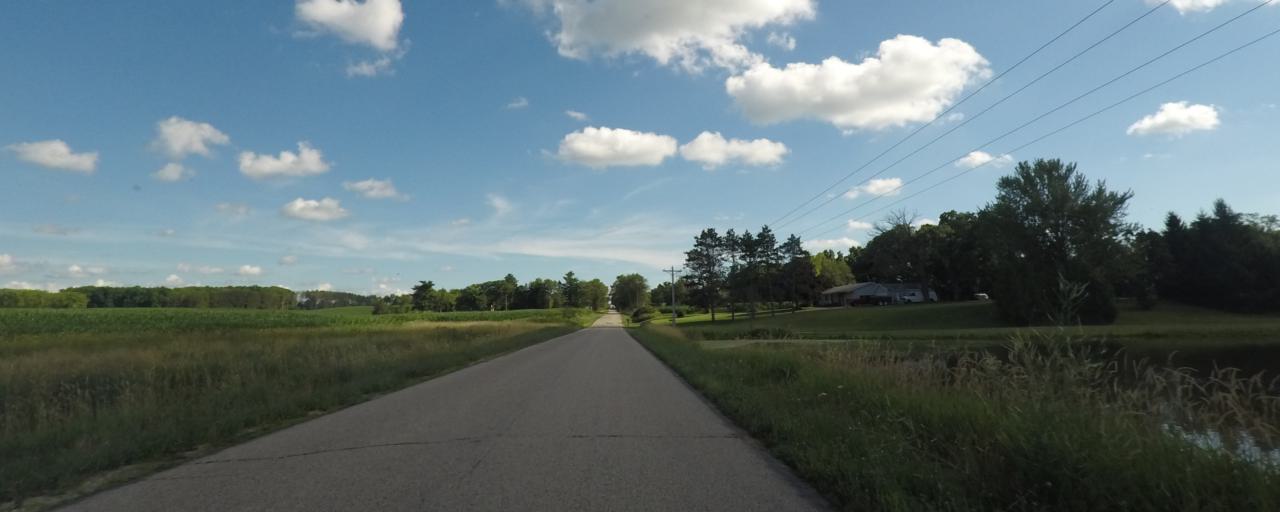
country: US
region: Wisconsin
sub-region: Rock County
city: Edgerton
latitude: 42.8352
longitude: -89.1320
